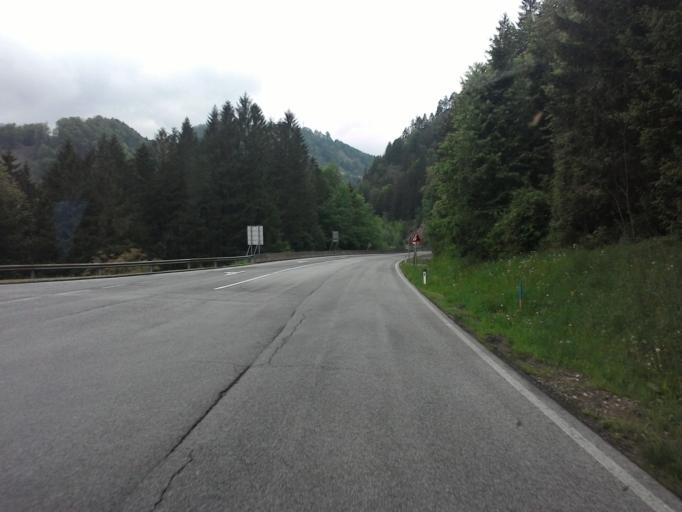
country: AT
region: Styria
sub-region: Politischer Bezirk Liezen
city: Altenmarkt bei Sankt Gallen
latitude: 47.7246
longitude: 14.6504
